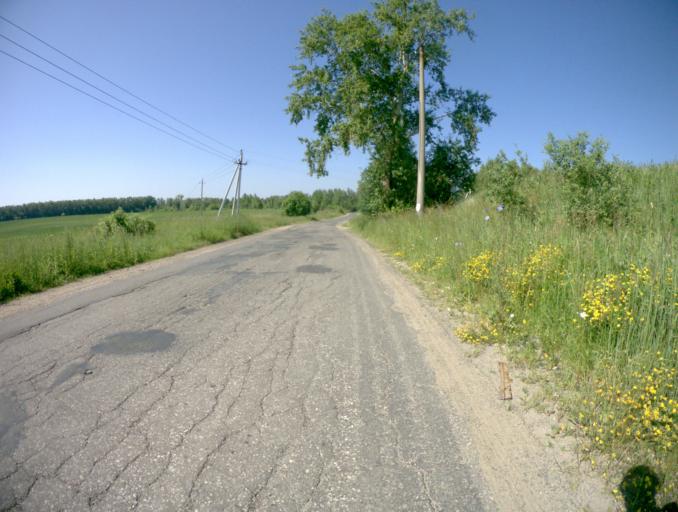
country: RU
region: Vladimir
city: Novovyazniki
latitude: 56.2317
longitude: 42.2166
